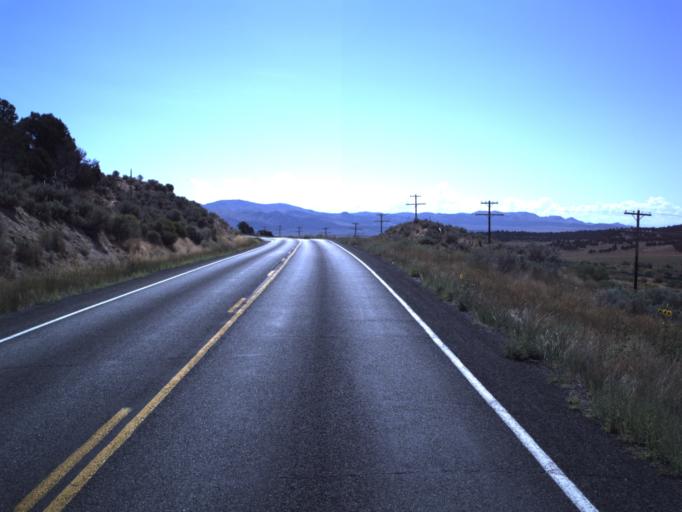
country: US
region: Utah
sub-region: Utah County
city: Genola
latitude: 39.9489
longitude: -112.2346
